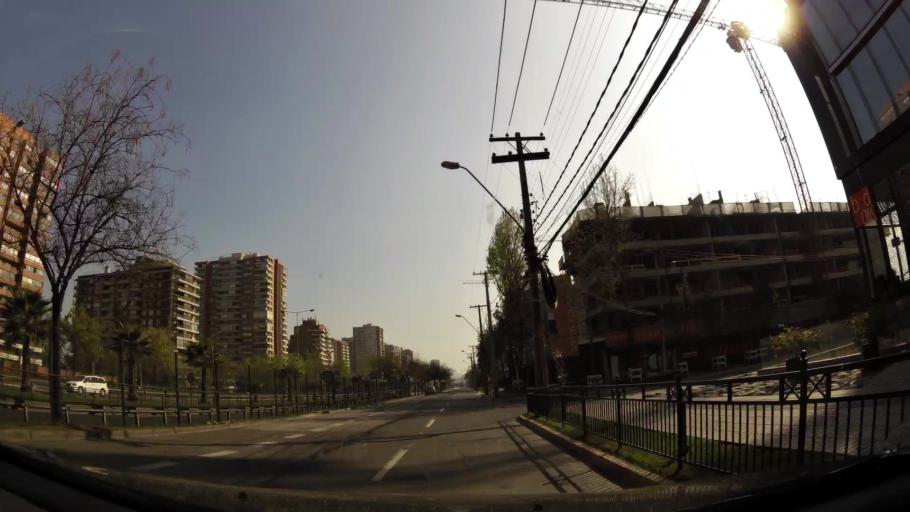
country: CL
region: Santiago Metropolitan
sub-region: Provincia de Santiago
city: Villa Presidente Frei, Nunoa, Santiago, Chile
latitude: -33.3924
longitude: -70.5561
